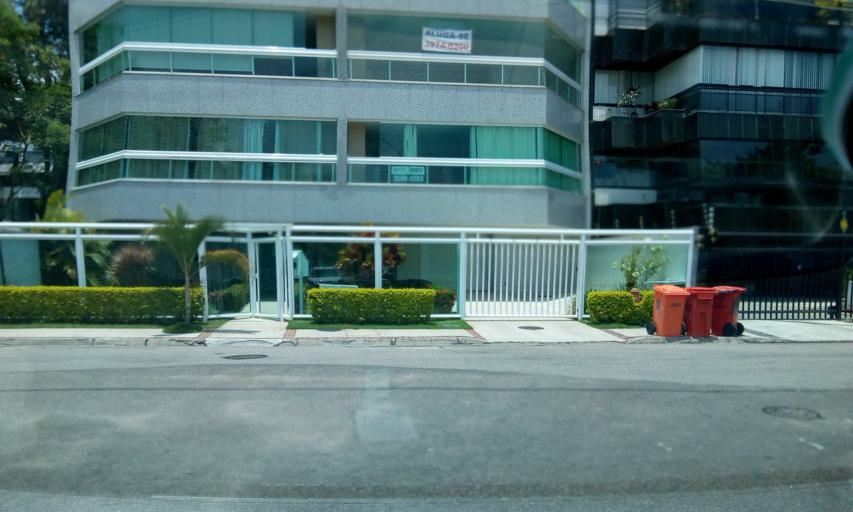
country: BR
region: Rio de Janeiro
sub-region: Nilopolis
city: Nilopolis
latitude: -23.0196
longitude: -43.4670
